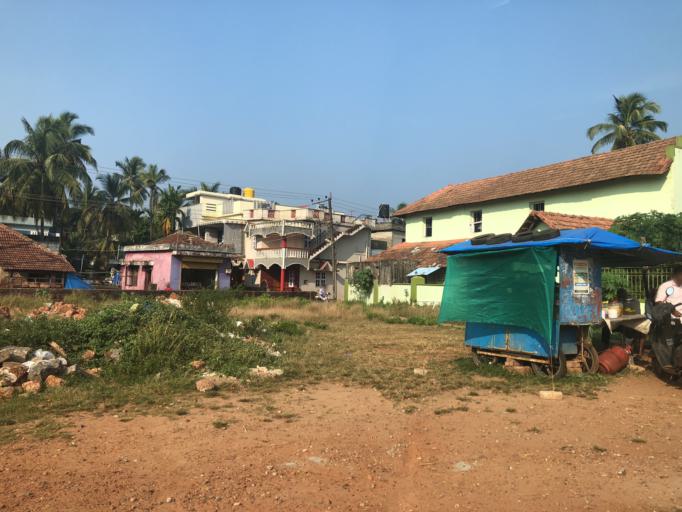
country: IN
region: Karnataka
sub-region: Dakshina Kannada
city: Ullal
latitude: 12.8200
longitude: 74.8460
